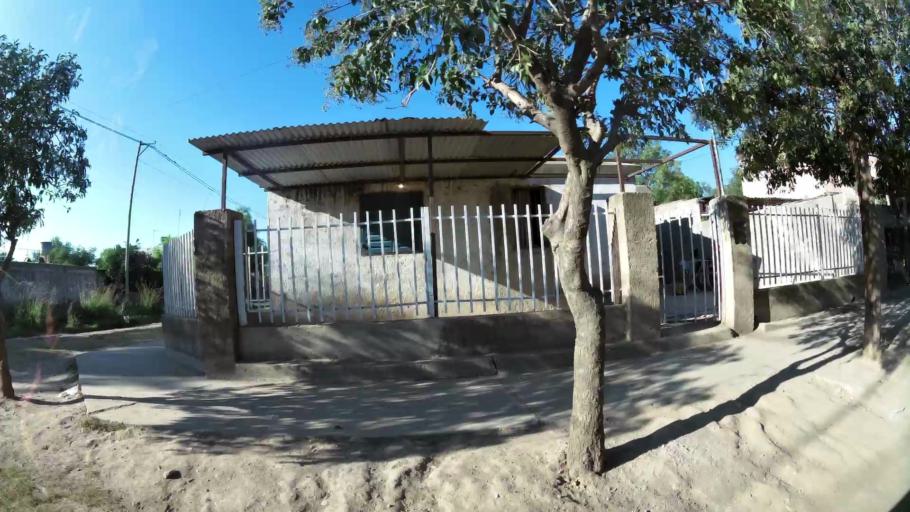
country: AR
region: Cordoba
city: Villa Allende
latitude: -31.3300
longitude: -64.2417
